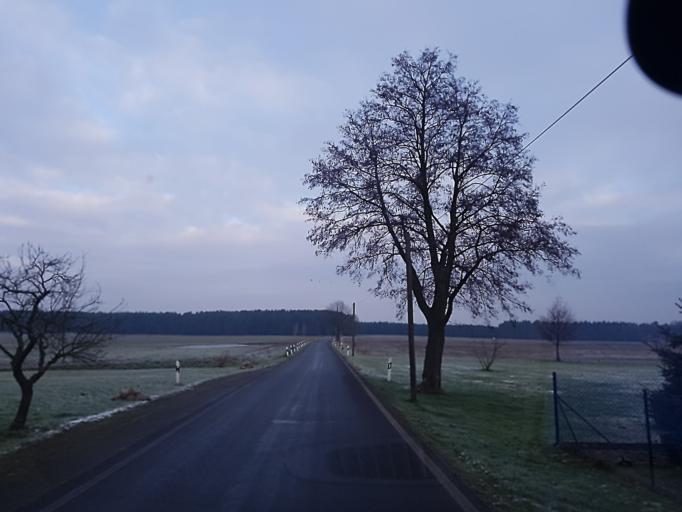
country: DE
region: Brandenburg
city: Crinitz
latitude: 51.7354
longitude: 13.8302
